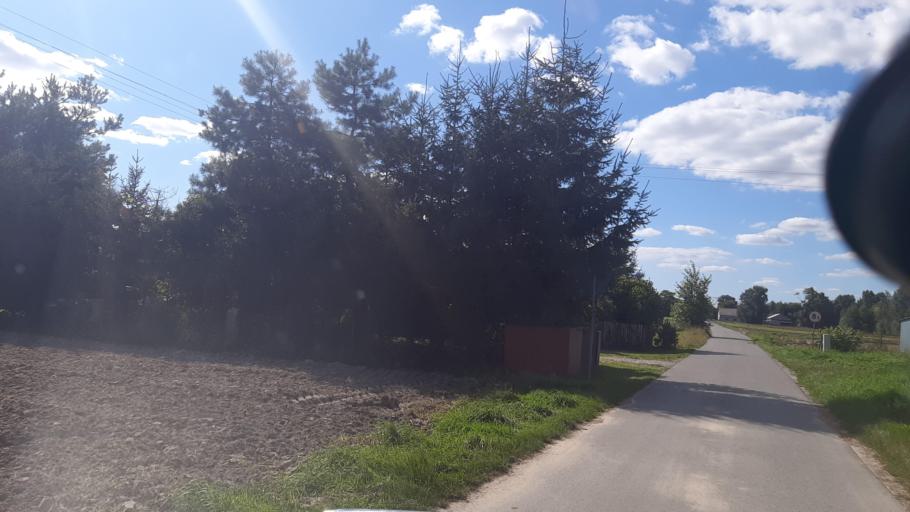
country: PL
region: Lublin Voivodeship
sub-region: Powiat pulawski
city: Markuszow
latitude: 51.3961
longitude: 22.2387
